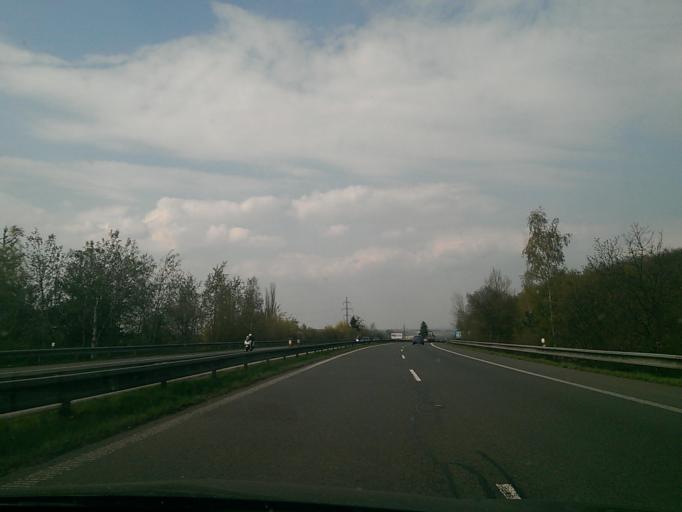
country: CZ
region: Central Bohemia
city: Kosmonosy
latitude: 50.4541
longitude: 14.9354
